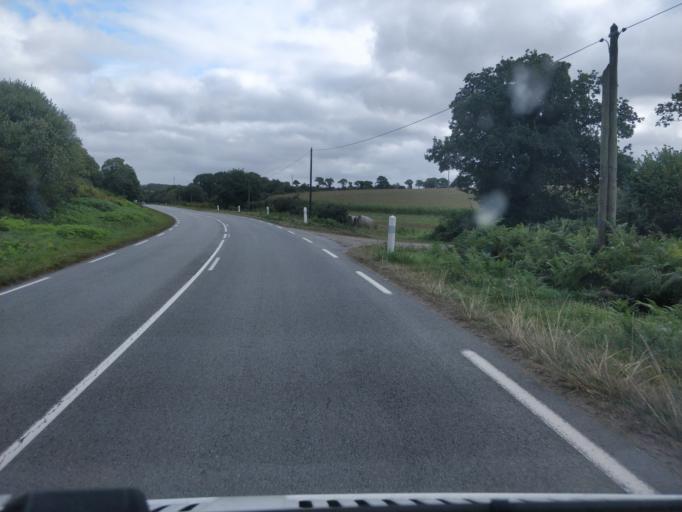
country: FR
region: Brittany
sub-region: Departement du Finistere
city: Ploneis
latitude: 47.9921
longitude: -4.2107
